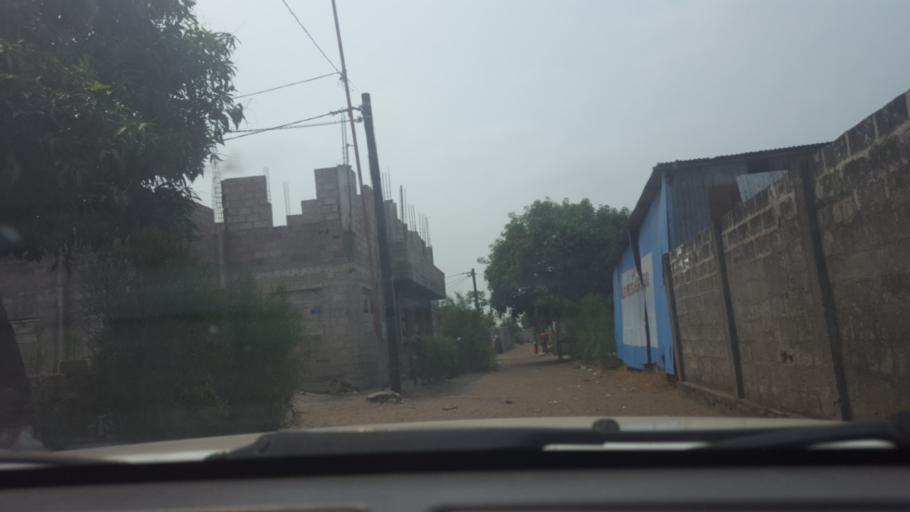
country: CD
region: Kinshasa
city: Masina
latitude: -4.3573
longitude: 15.5105
